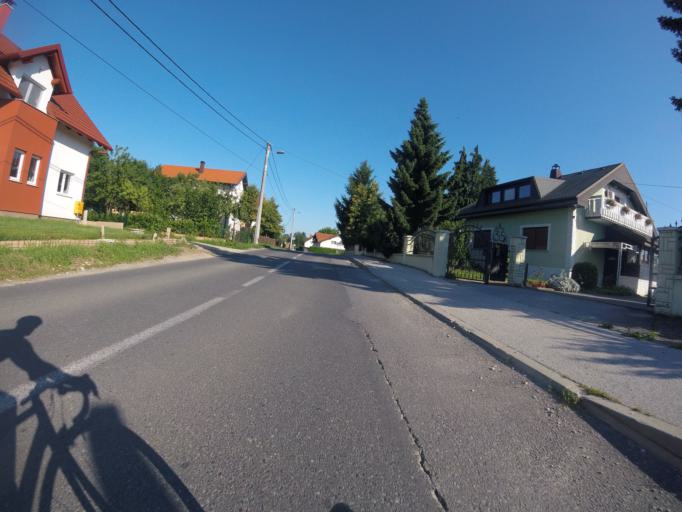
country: HR
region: Grad Zagreb
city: Zadvorsko
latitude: 45.7255
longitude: 15.9190
